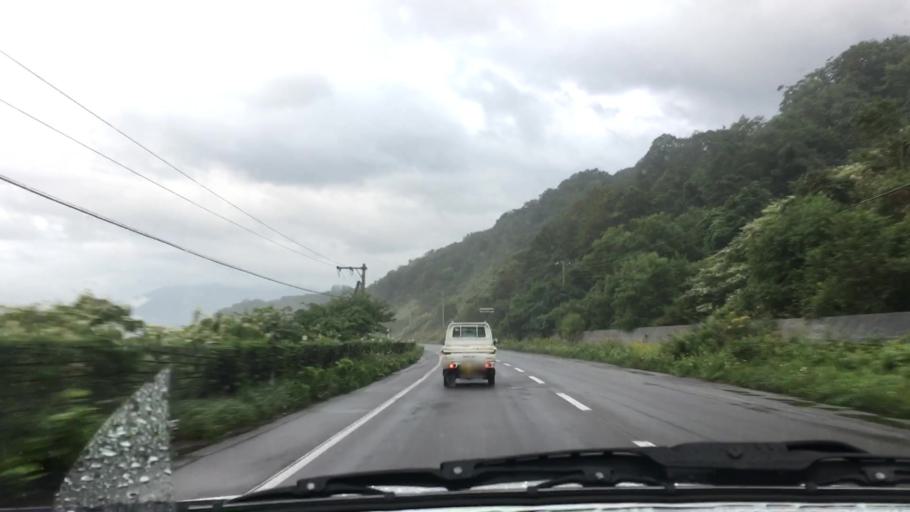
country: JP
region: Hokkaido
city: Nanae
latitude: 42.1260
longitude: 140.5185
